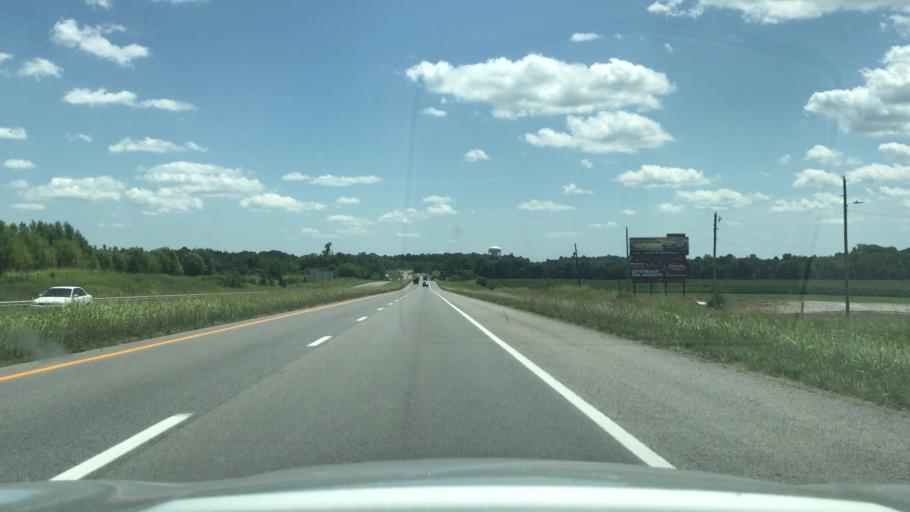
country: US
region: Kentucky
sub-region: Christian County
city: Hopkinsville
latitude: 36.8903
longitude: -87.4691
